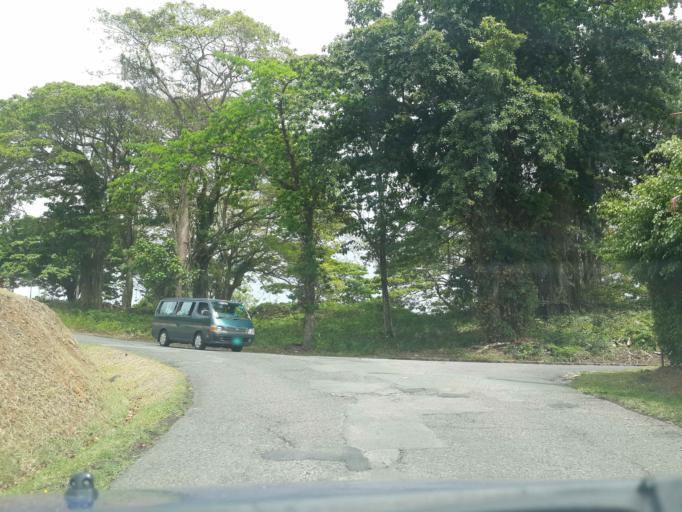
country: LC
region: Castries Quarter
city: Castries
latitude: 14.0000
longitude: -60.9982
